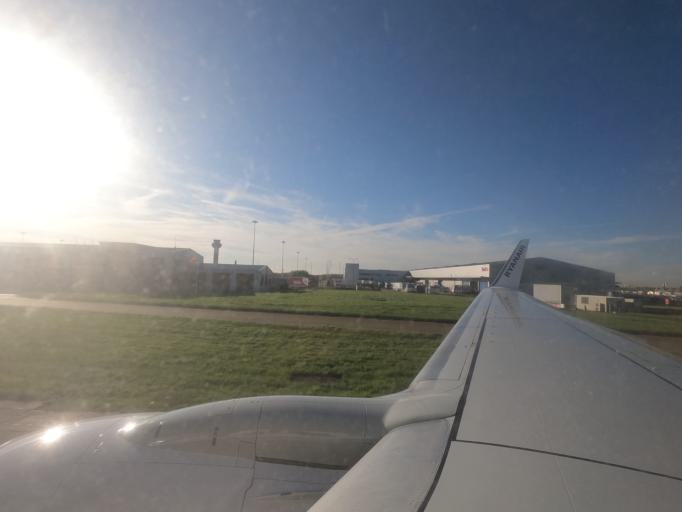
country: GB
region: England
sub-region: Essex
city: Takeley
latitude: 51.8877
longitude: 0.2466
